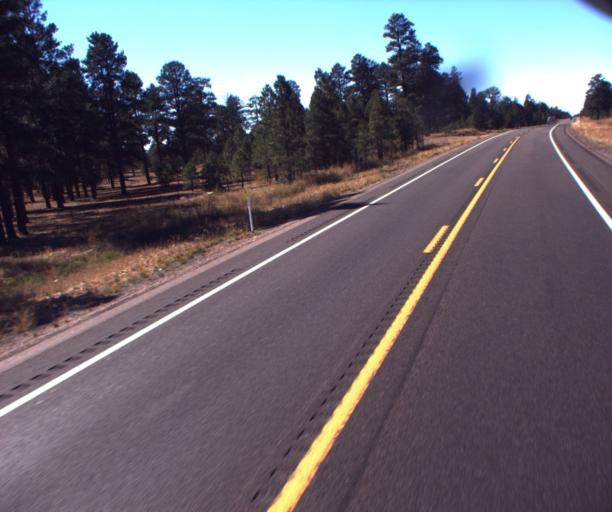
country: US
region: Arizona
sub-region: Apache County
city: Saint Michaels
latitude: 35.6860
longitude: -109.2401
